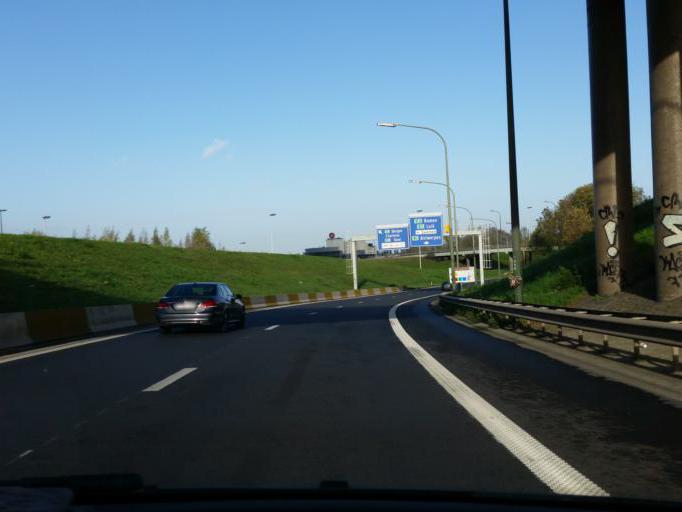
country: BE
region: Flanders
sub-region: Provincie Vlaams-Brabant
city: Bever
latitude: 50.9114
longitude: 4.3441
